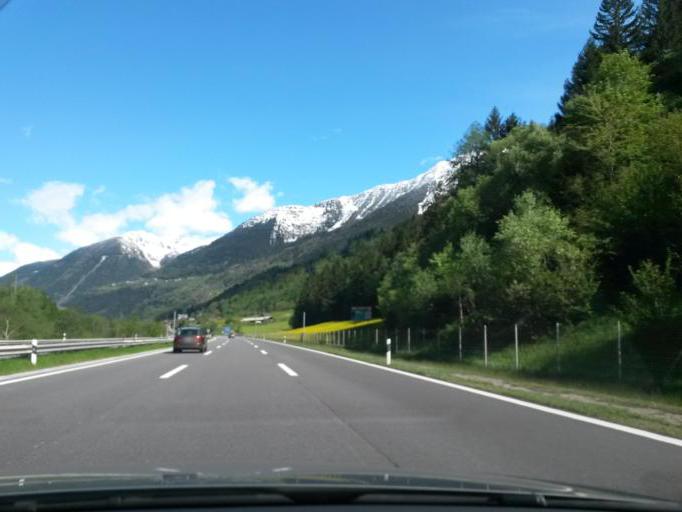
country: CH
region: Ticino
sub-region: Leventina District
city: Faido
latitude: 46.4956
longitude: 8.7354
